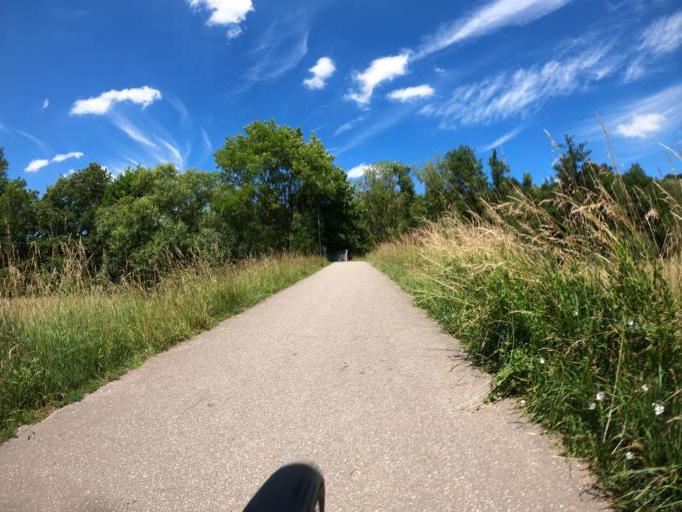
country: DE
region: Baden-Wuerttemberg
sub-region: Regierungsbezirk Stuttgart
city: Bietigheim-Bissingen
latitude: 48.9475
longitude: 9.0898
